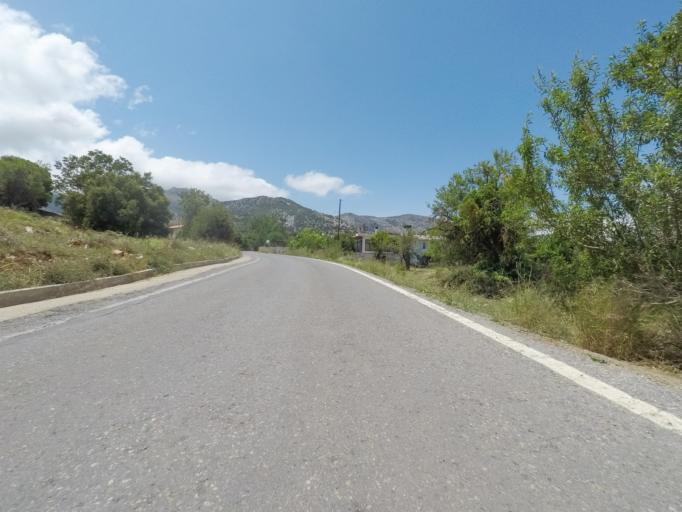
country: GR
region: Crete
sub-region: Nomos Irakleiou
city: Mokhos
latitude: 35.1703
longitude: 25.4447
